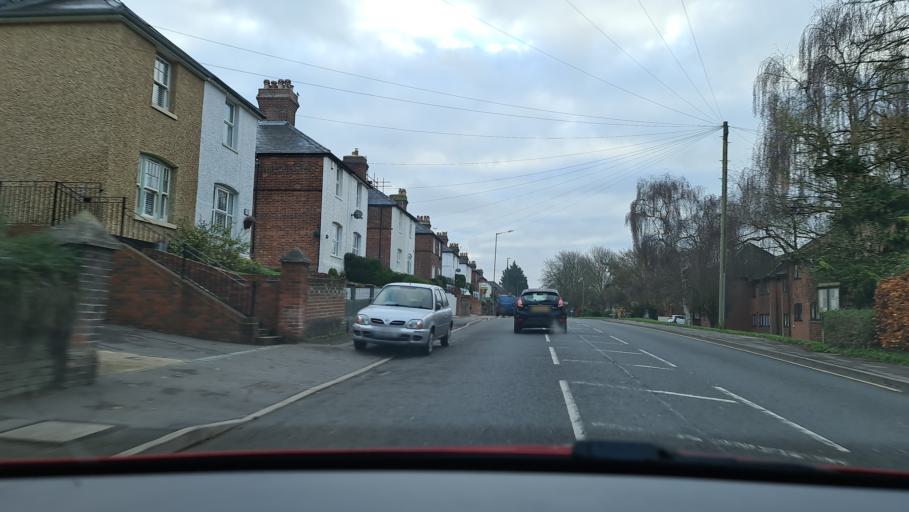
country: GB
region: England
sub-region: Buckinghamshire
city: High Wycombe
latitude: 51.6437
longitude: -0.7934
